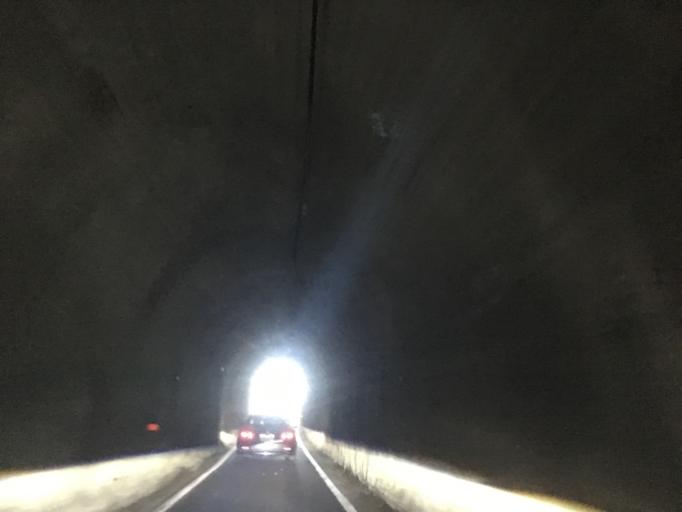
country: TW
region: Taiwan
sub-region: Hualien
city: Hualian
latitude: 24.1887
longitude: 121.3473
